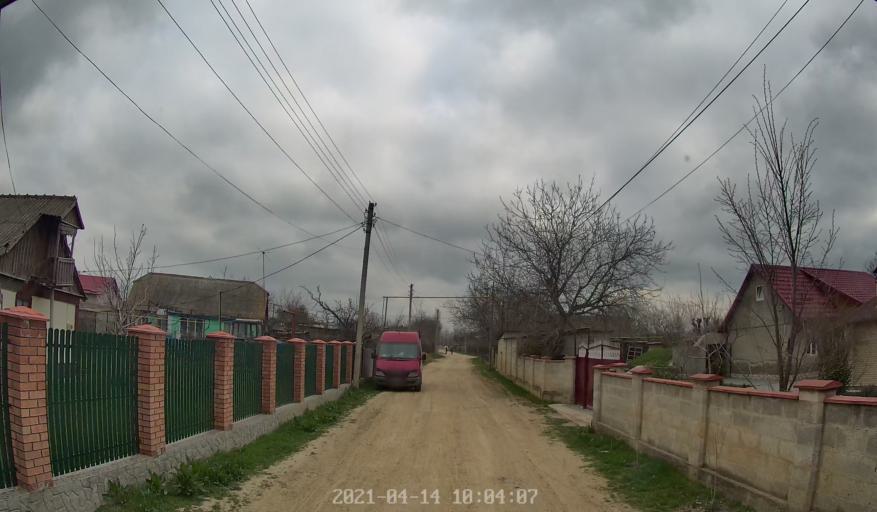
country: MD
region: Chisinau
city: Vadul lui Voda
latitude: 47.1443
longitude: 29.1257
